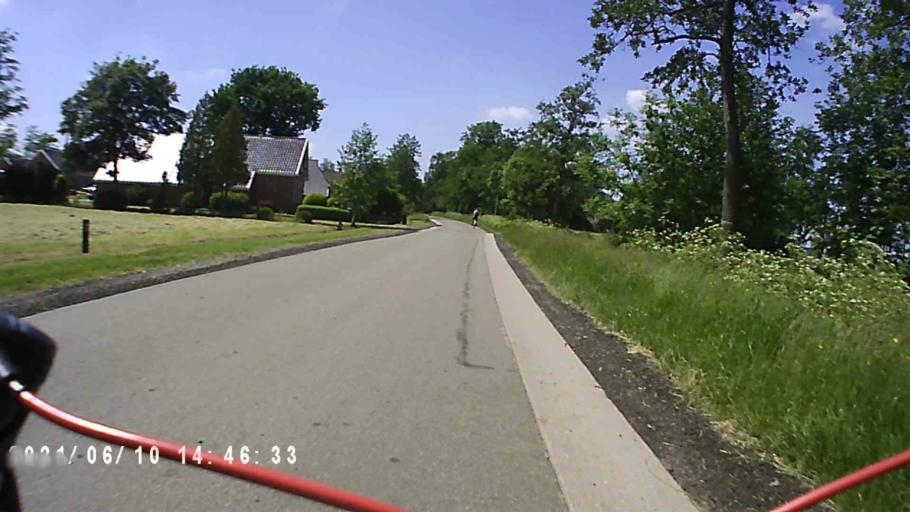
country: NL
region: Groningen
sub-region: Gemeente Grootegast
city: Grootegast
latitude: 53.2363
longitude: 6.2718
